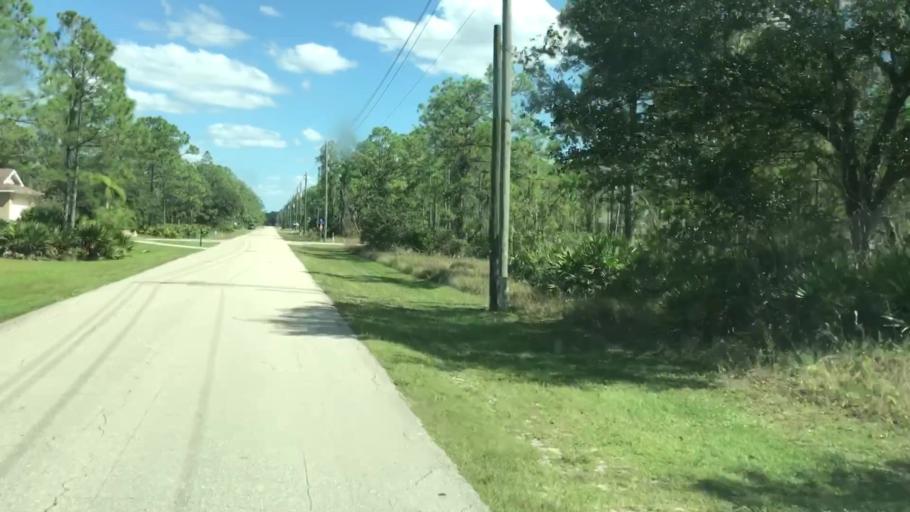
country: US
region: Florida
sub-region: Lee County
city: Alva
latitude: 26.6835
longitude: -81.5934
